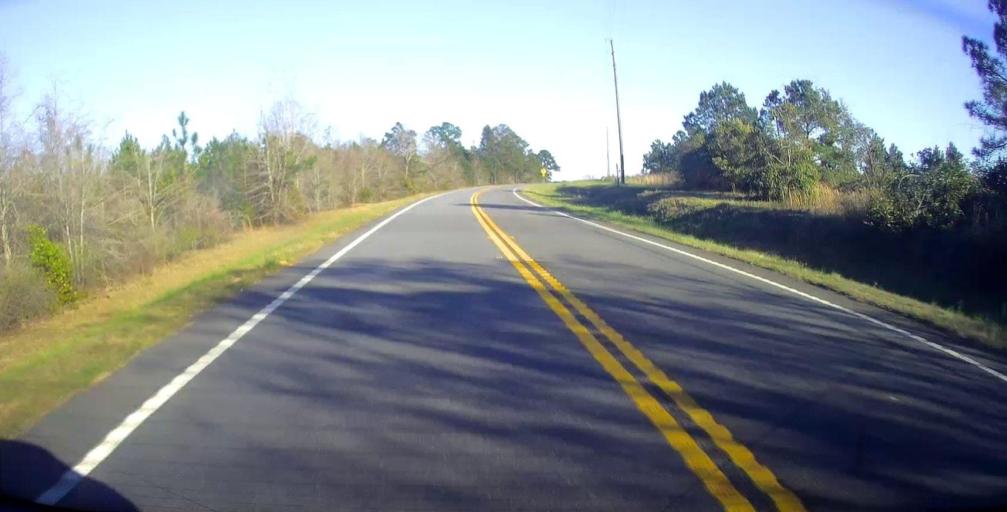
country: US
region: Georgia
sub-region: Taylor County
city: Butler
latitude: 32.5003
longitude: -84.4075
